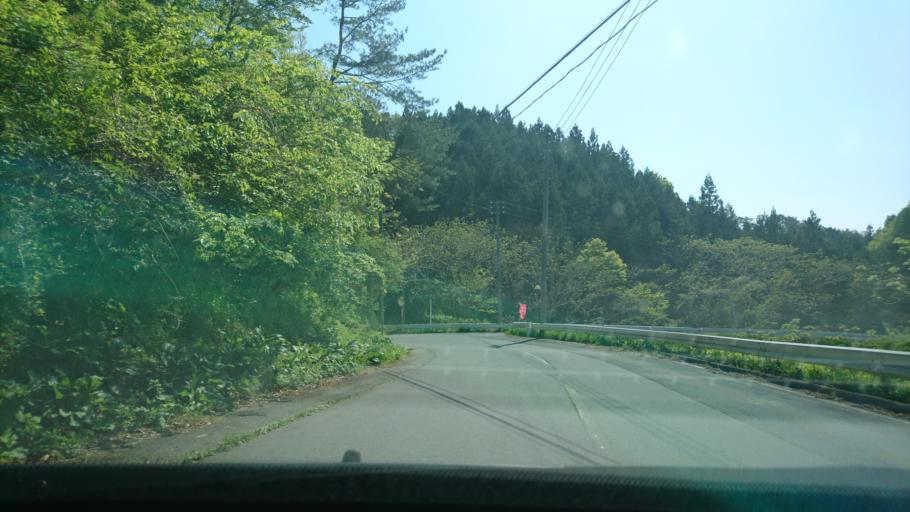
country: JP
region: Iwate
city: Ichinoseki
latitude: 38.9334
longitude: 141.2789
